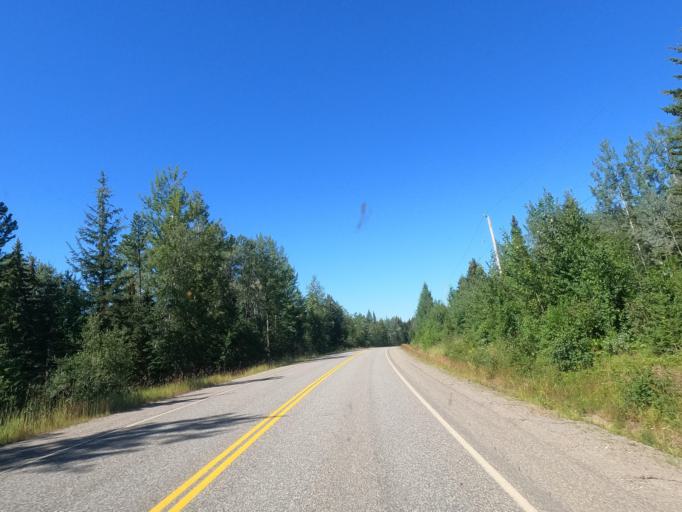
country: CA
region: British Columbia
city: Quesnel
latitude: 53.0282
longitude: -122.0166
